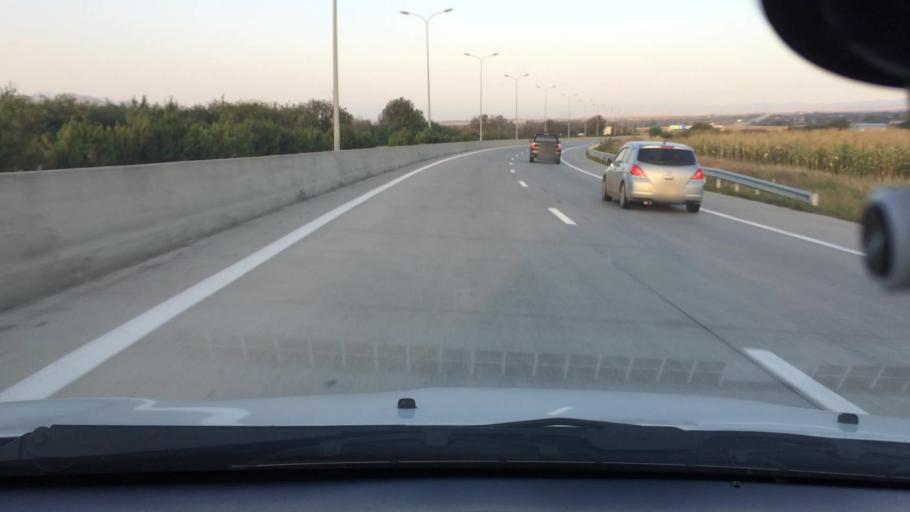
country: GE
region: Shida Kartli
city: Gori
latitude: 42.0175
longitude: 43.9912
